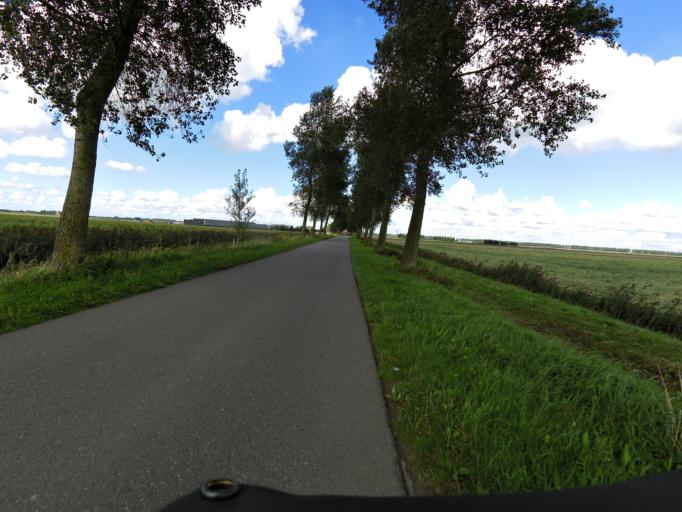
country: NL
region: South Holland
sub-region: Gemeente Goeree-Overflakkee
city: Middelharnis
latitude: 51.7087
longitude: 4.2338
